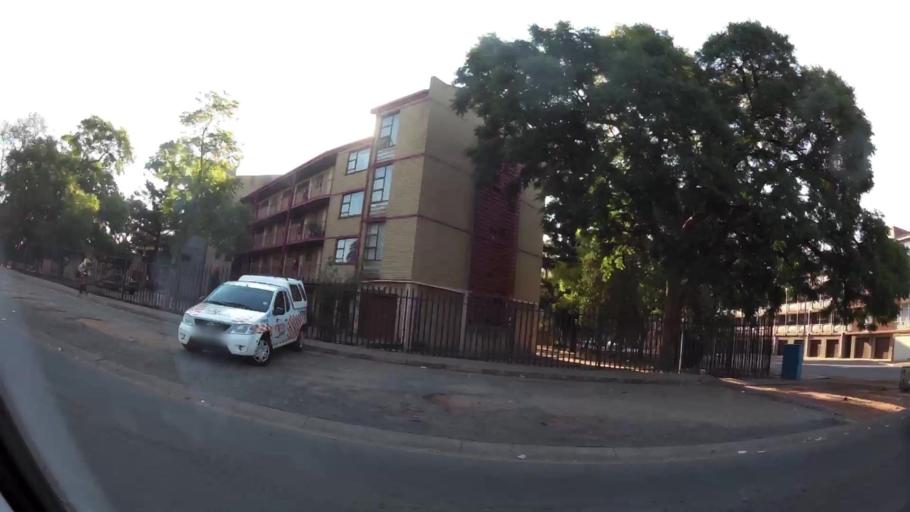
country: ZA
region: North-West
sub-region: Bojanala Platinum District Municipality
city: Rustenburg
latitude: -25.6734
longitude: 27.2397
